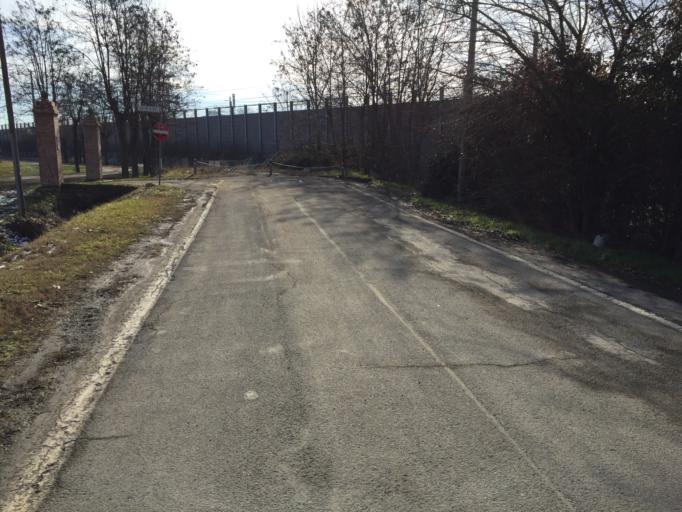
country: IT
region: Emilia-Romagna
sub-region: Provincia di Bologna
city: Calderara di Reno
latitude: 44.5233
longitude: 11.2762
